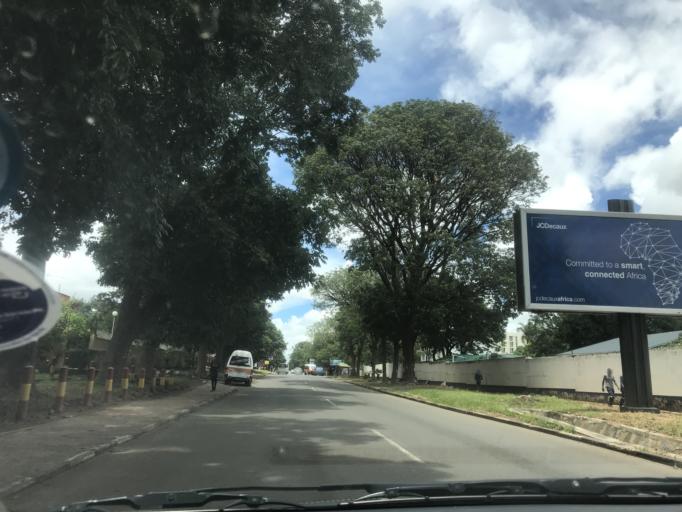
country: ZM
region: Lusaka
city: Lusaka
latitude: -15.4182
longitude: 28.3114
